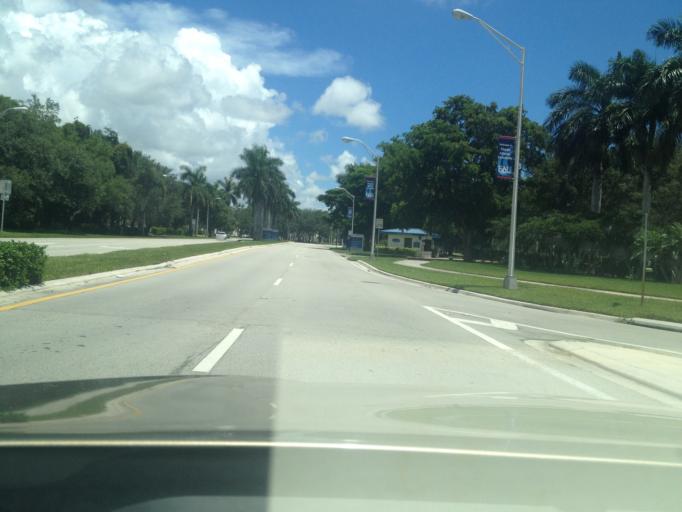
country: US
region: Florida
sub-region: Palm Beach County
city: Boca Raton
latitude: 26.3657
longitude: -80.1060
